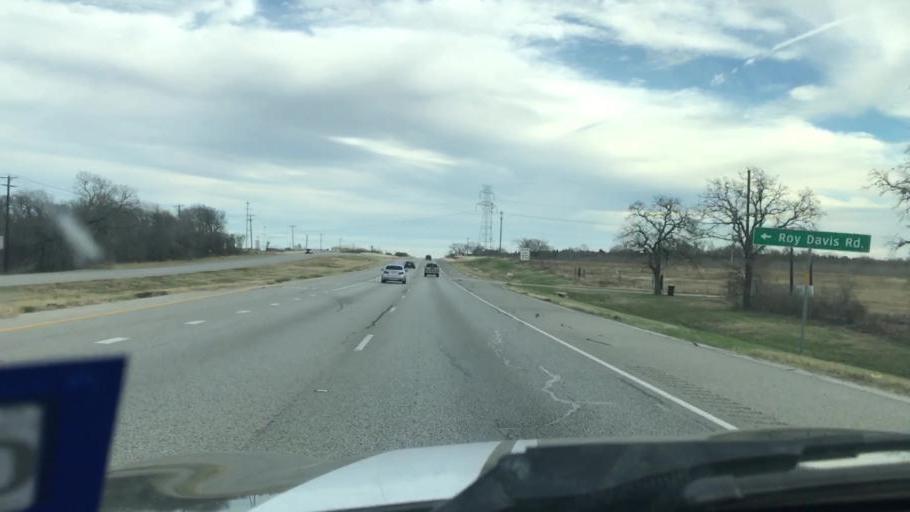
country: US
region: Texas
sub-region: Bastrop County
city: Elgin
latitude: 30.3318
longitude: -97.3510
